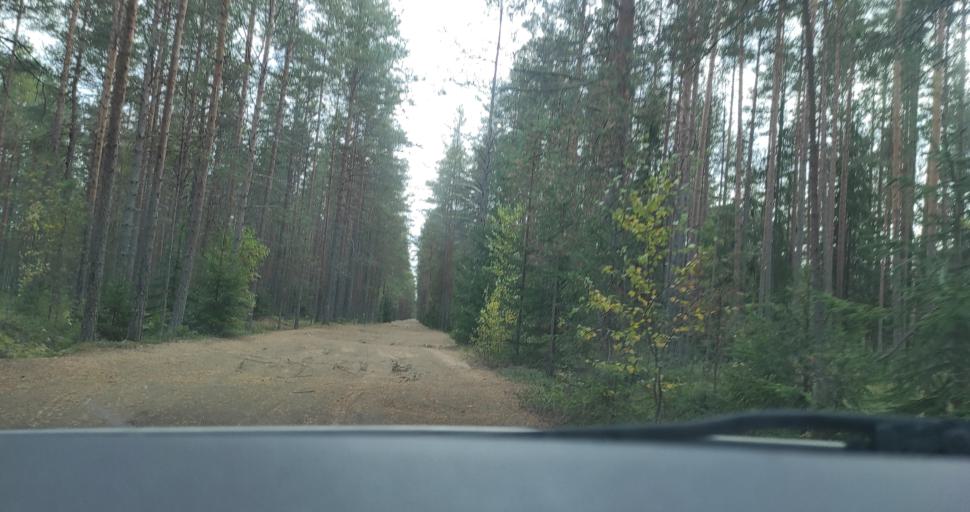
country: RU
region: Leningrad
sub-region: Vsevolzhskij Rajon
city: Vaskelovo
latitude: 60.4123
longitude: 30.3287
